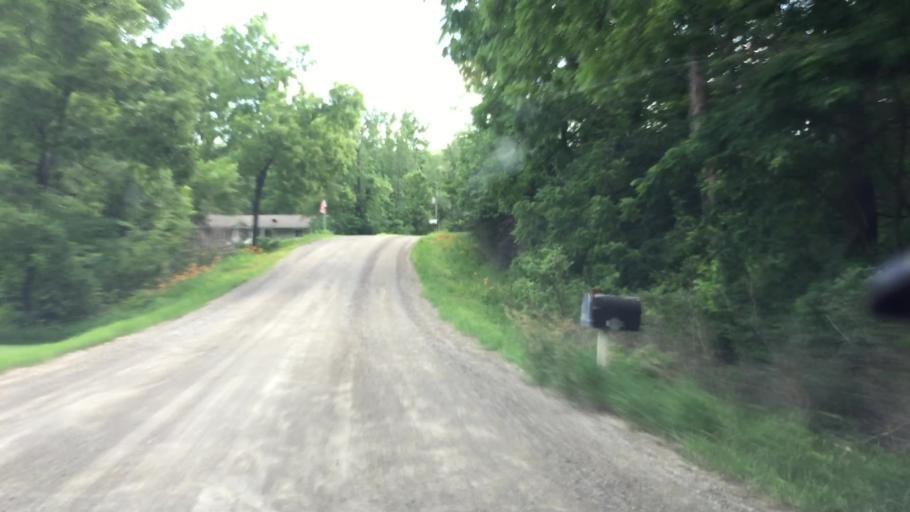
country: US
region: Iowa
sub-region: Linn County
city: Ely
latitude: 41.8327
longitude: -91.6122
